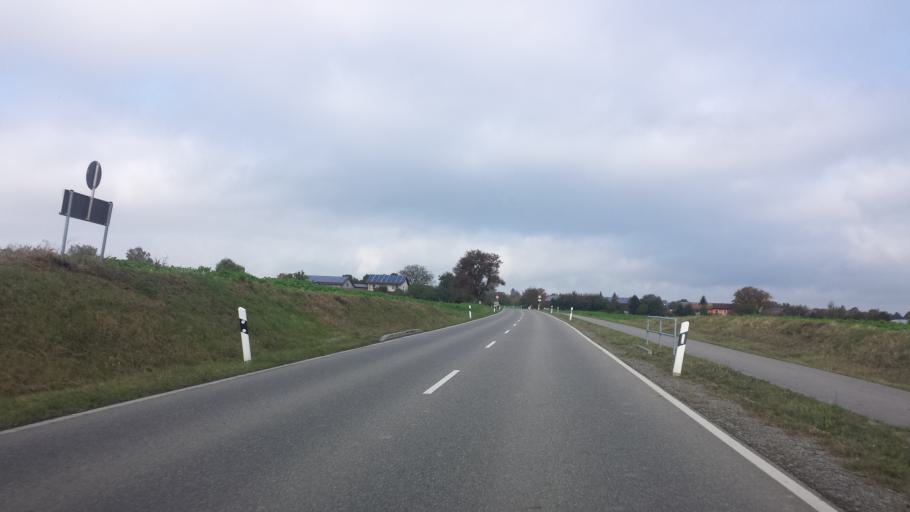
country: DE
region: Baden-Wuerttemberg
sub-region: Regierungsbezirk Stuttgart
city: Bad Rappenau
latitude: 49.2254
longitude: 9.1071
